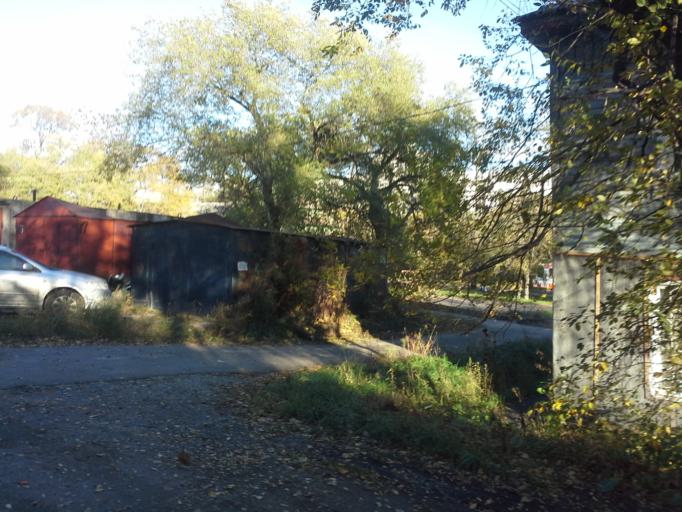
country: RU
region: Khabarovsk Krai
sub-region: Khabarovskiy Rayon
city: Khabarovsk
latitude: 48.4856
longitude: 135.0639
